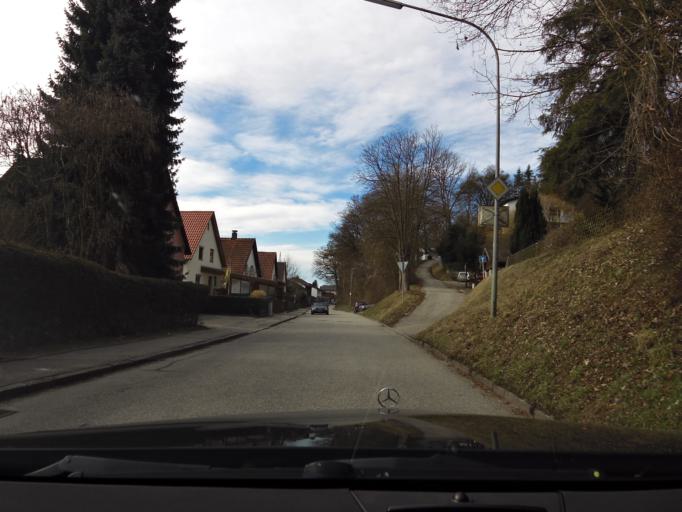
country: DE
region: Bavaria
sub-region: Lower Bavaria
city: Tiefenbach
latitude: 48.5515
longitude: 12.0970
